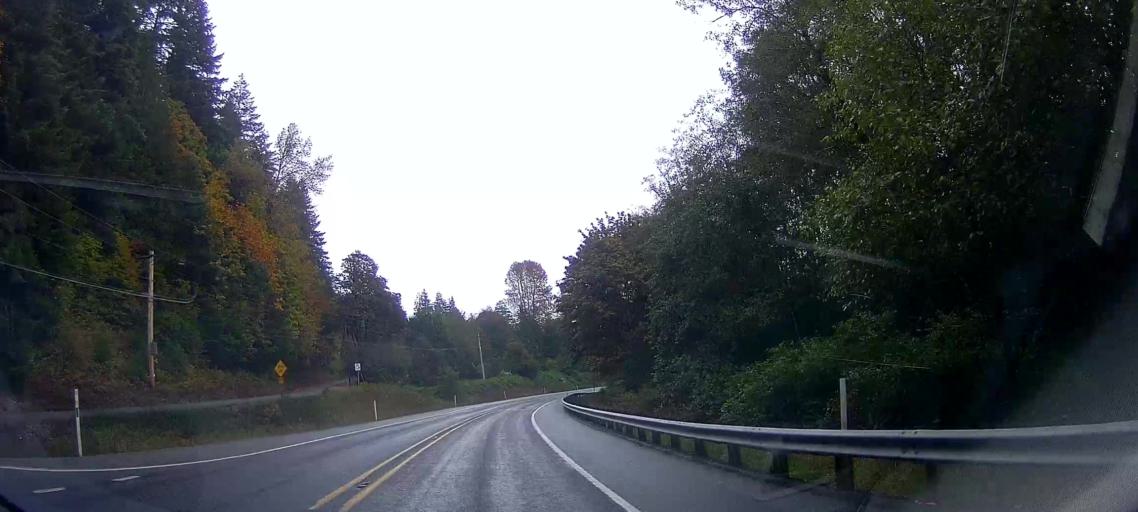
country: US
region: Washington
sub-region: Snohomish County
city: Darrington
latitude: 48.5415
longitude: -121.8150
